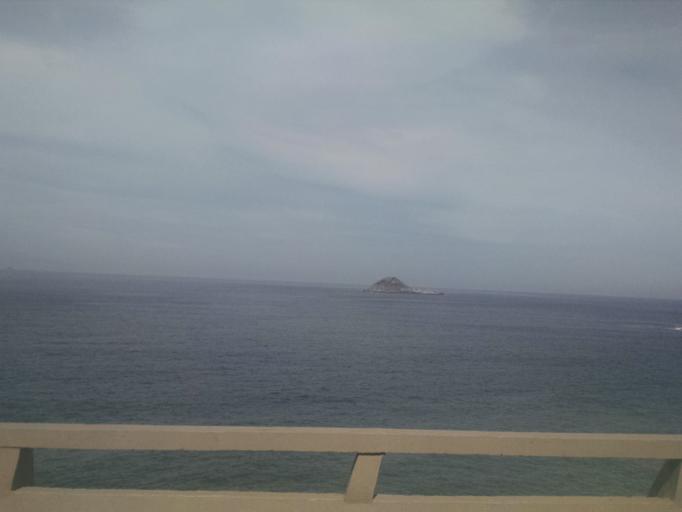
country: BR
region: Rio de Janeiro
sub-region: Rio De Janeiro
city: Rio de Janeiro
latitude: -23.0082
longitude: -43.2855
